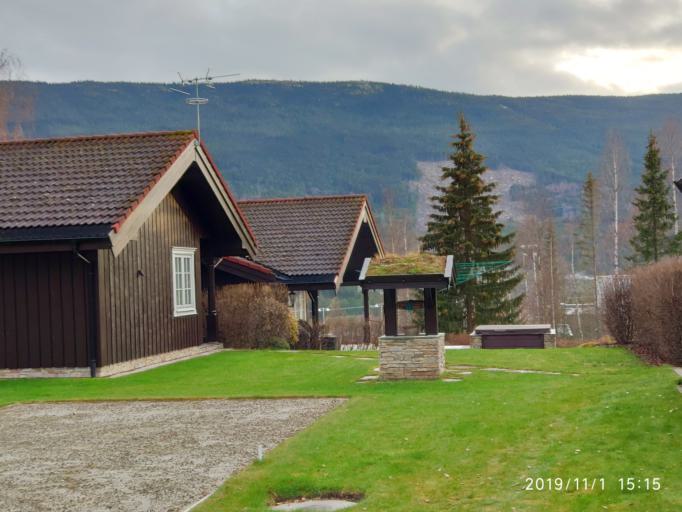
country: NO
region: Buskerud
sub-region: Gol
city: Gol
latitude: 60.7065
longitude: 8.9416
